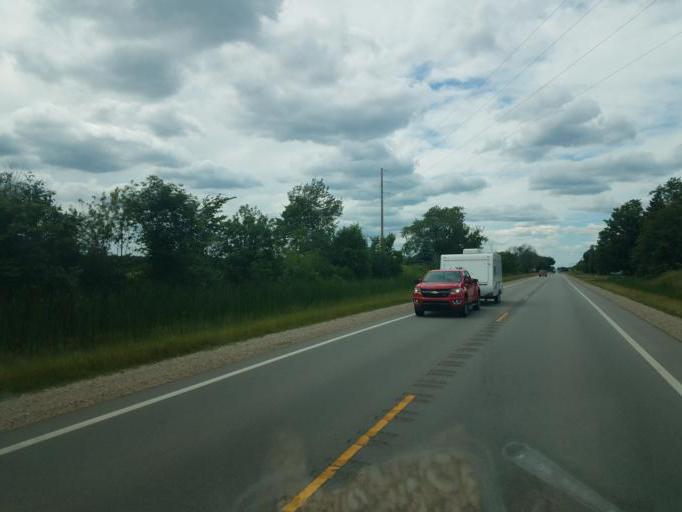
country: US
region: Michigan
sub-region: Eaton County
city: Charlotte
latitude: 42.6598
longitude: -84.9122
